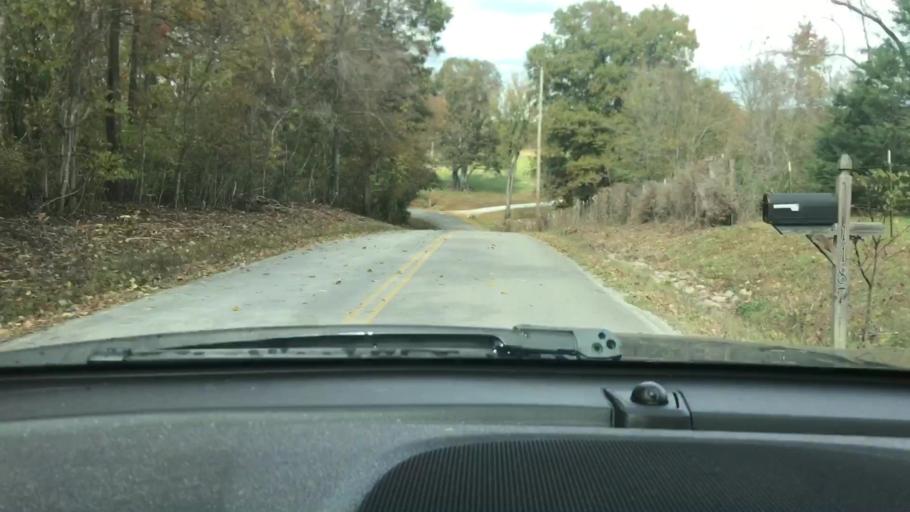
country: US
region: Tennessee
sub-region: Dickson County
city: Charlotte
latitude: 36.1918
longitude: -87.2890
